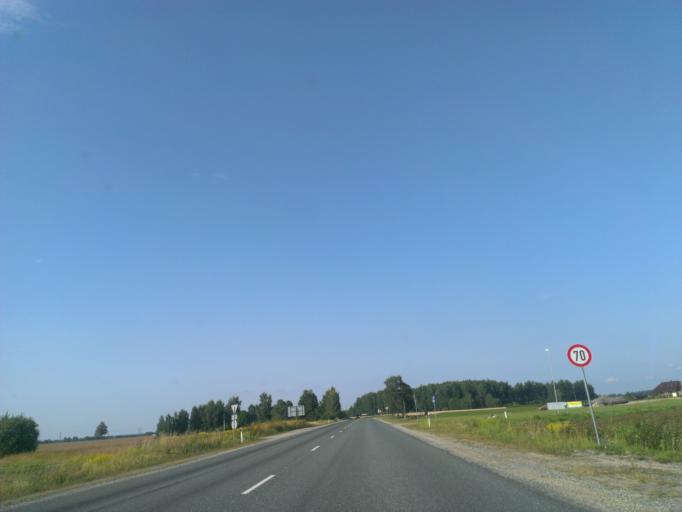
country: LV
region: Priekuli
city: Priekuli
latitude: 57.3145
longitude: 25.3199
